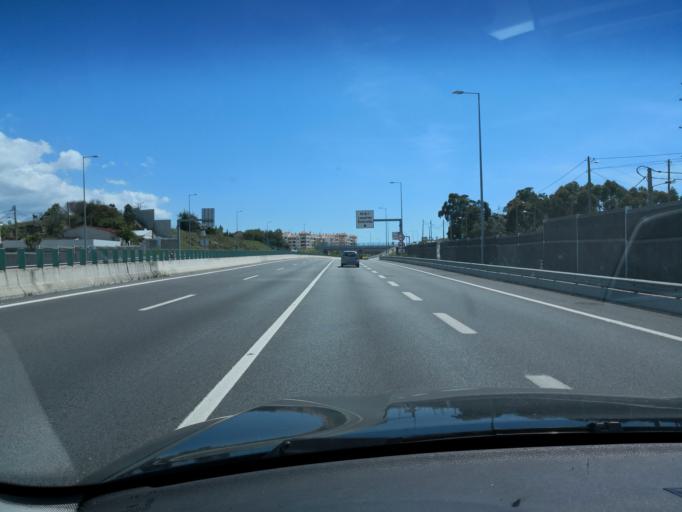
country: PT
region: Setubal
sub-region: Almada
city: Sobreda
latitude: 38.6504
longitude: -9.2010
